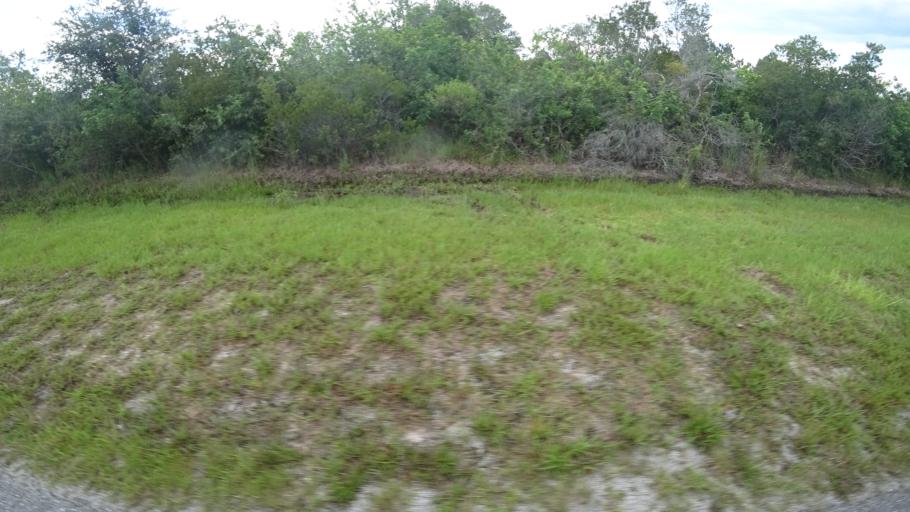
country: US
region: Florida
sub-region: Sarasota County
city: The Meadows
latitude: 27.4148
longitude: -82.2792
